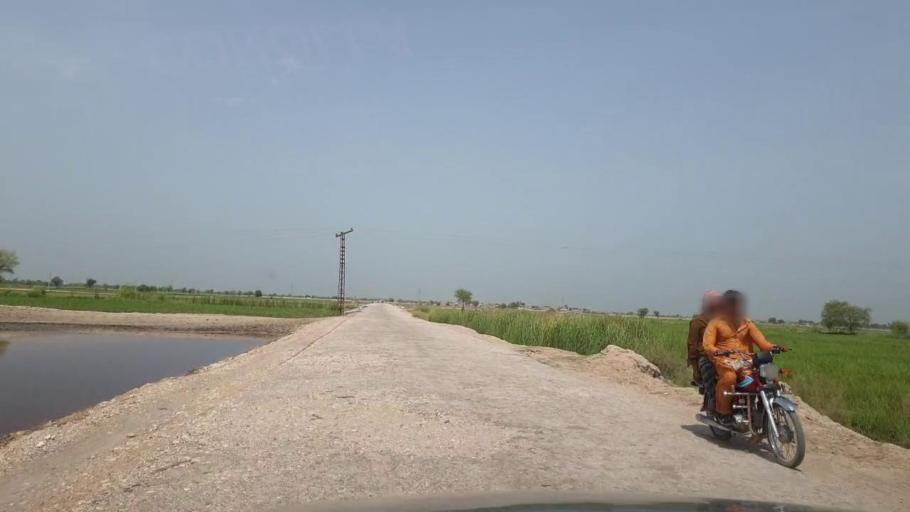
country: PK
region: Sindh
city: Garhi Yasin
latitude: 27.8535
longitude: 68.4373
